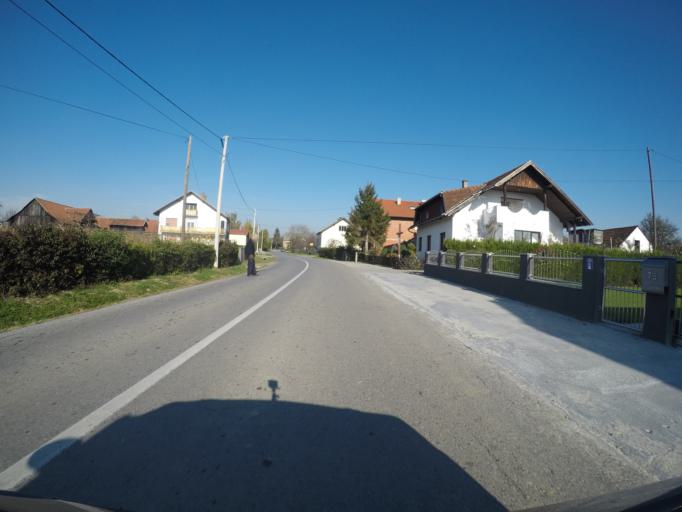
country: HR
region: Bjelovarsko-Bilogorska
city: Predavac
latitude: 45.9205
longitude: 16.7886
